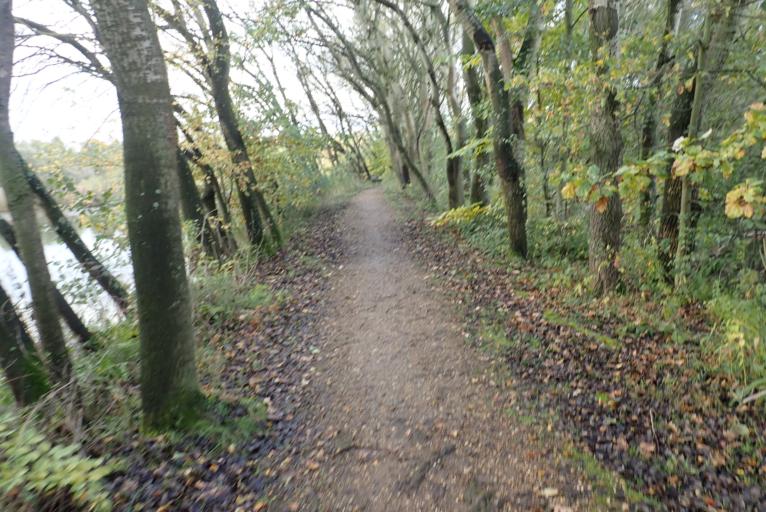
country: BE
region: Flanders
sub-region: Provincie Antwerpen
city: Niel
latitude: 51.1058
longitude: 4.3434
